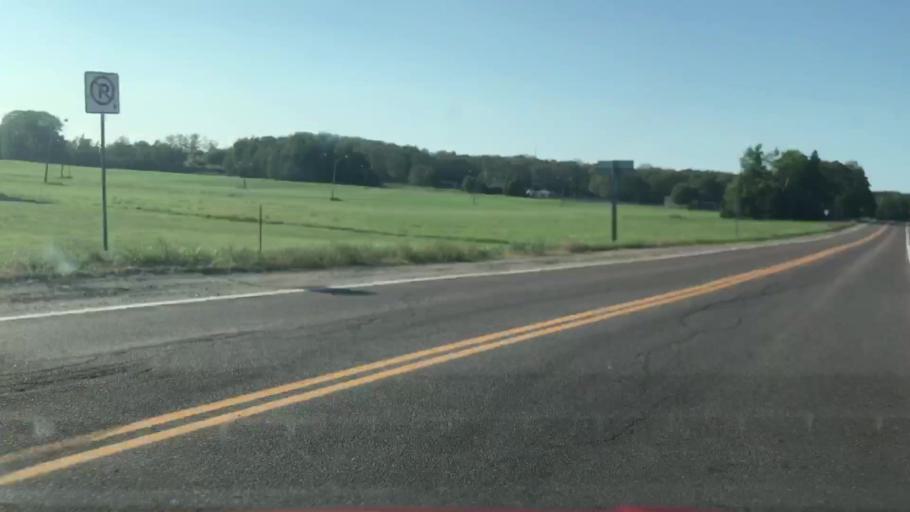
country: US
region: Michigan
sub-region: Chippewa County
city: Sault Ste. Marie
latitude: 46.2760
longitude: -84.0278
